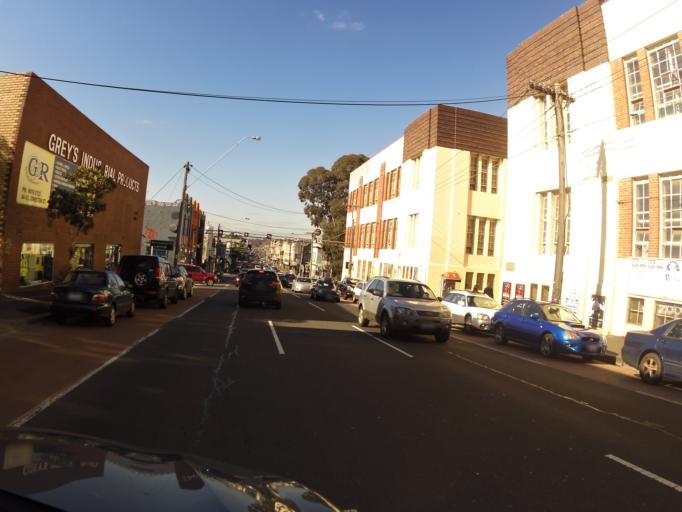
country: AU
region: Victoria
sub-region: Yarra
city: Collingwood
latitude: -37.7991
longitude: 144.9860
